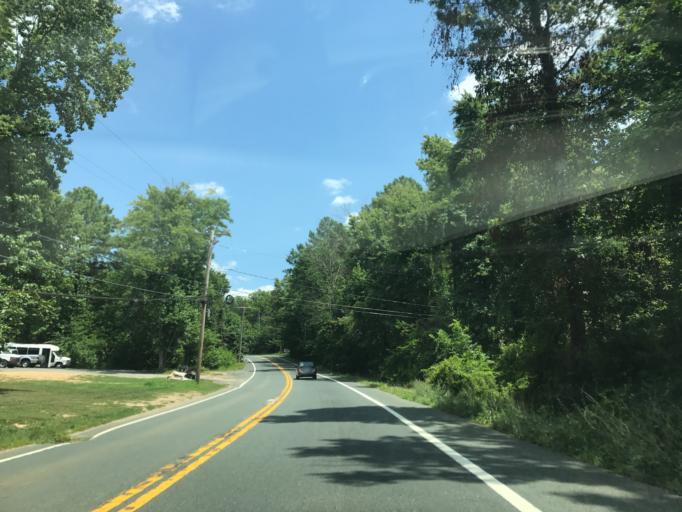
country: US
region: Maryland
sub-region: Prince George's County
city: South Laurel
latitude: 39.0464
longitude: -76.8273
